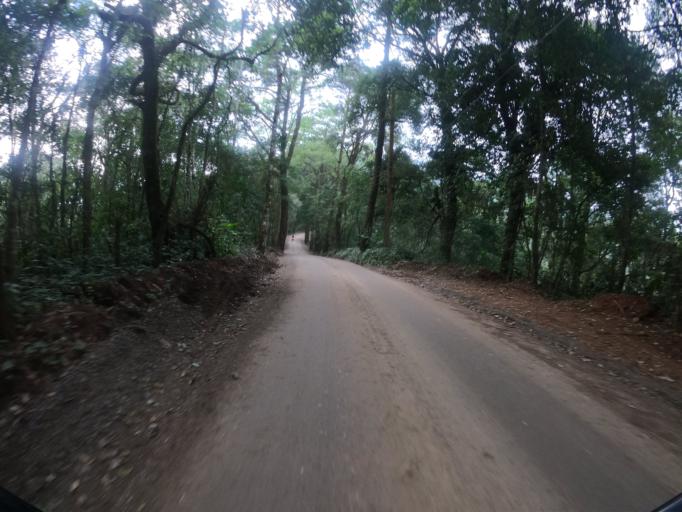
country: TH
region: Chiang Mai
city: Chiang Mai
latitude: 18.8216
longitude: 98.8908
